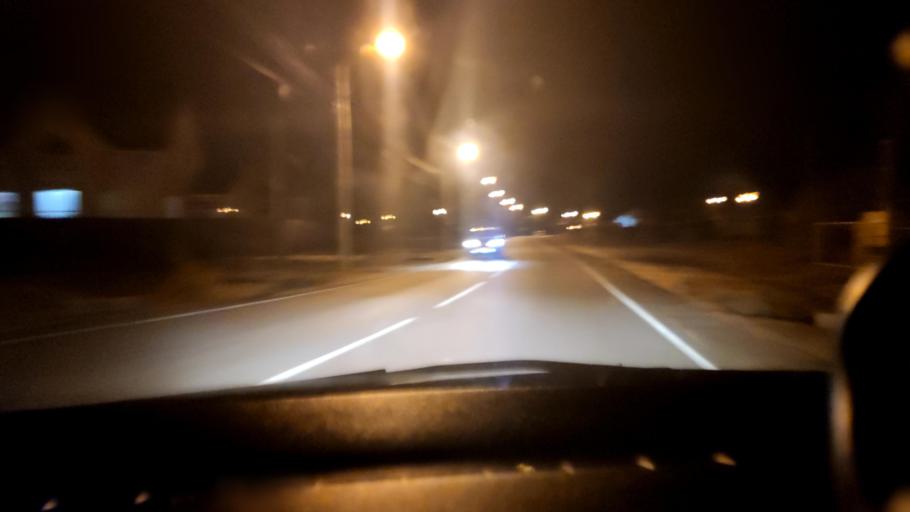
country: RU
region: Voronezj
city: Shilovo
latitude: 51.5490
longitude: 39.0866
